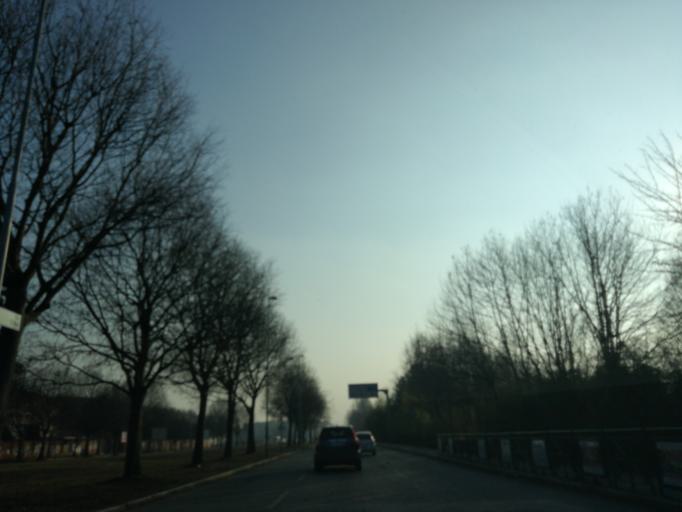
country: IT
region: Piedmont
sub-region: Provincia di Torino
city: Lesna
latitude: 45.0532
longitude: 7.6149
